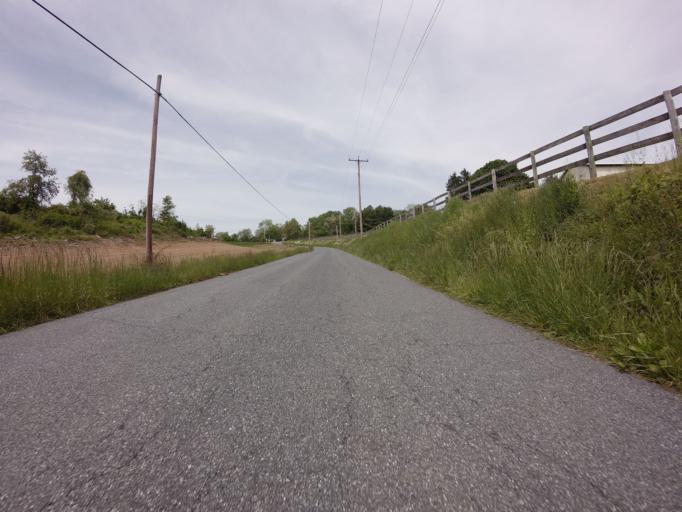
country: US
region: Maryland
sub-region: Carroll County
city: Westminster
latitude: 39.4885
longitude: -77.0028
